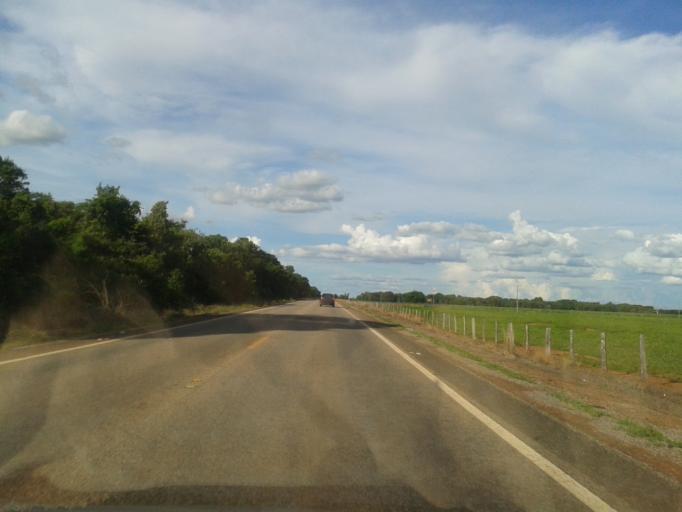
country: BR
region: Goias
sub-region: Mozarlandia
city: Mozarlandia
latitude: -14.3248
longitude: -50.4116
